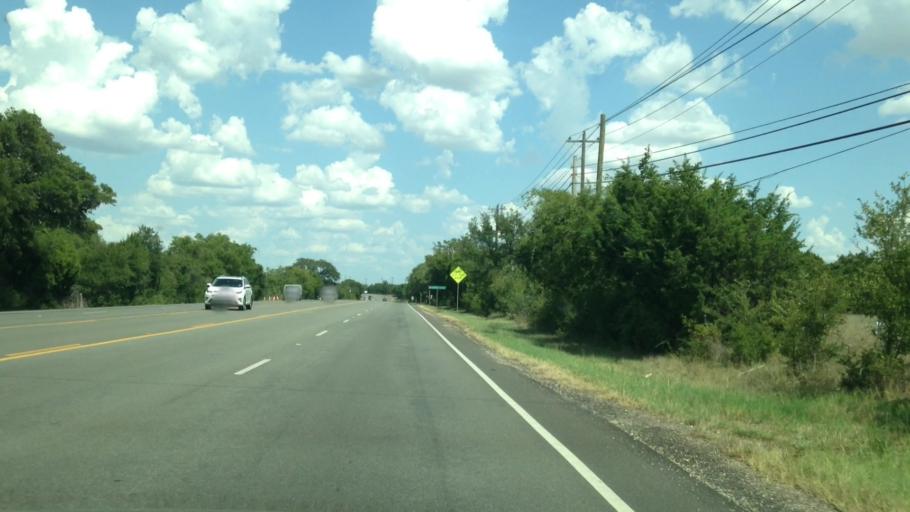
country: US
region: Texas
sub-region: Williamson County
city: Georgetown
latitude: 30.6314
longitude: -97.7510
